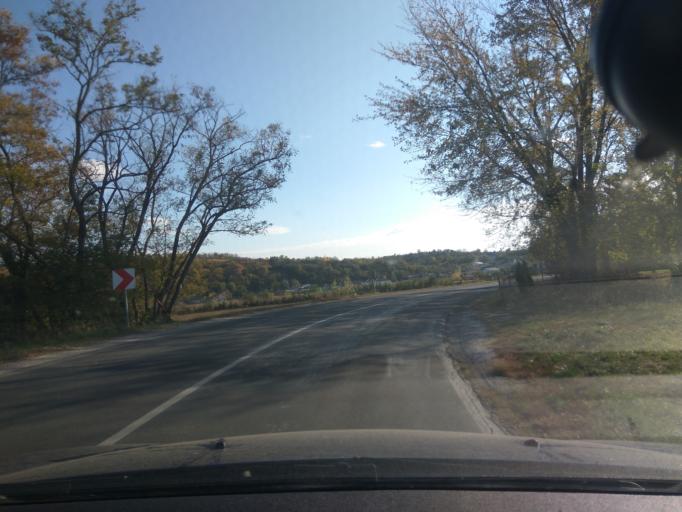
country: SK
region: Trnavsky
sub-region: Okres Trnava
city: Piestany
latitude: 48.5683
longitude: 17.8395
